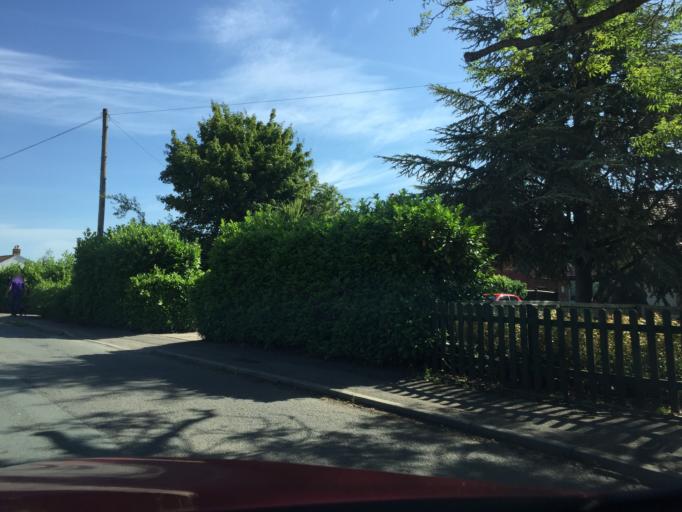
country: GB
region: England
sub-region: Gloucestershire
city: Stonehouse
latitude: 51.8174
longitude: -2.2936
